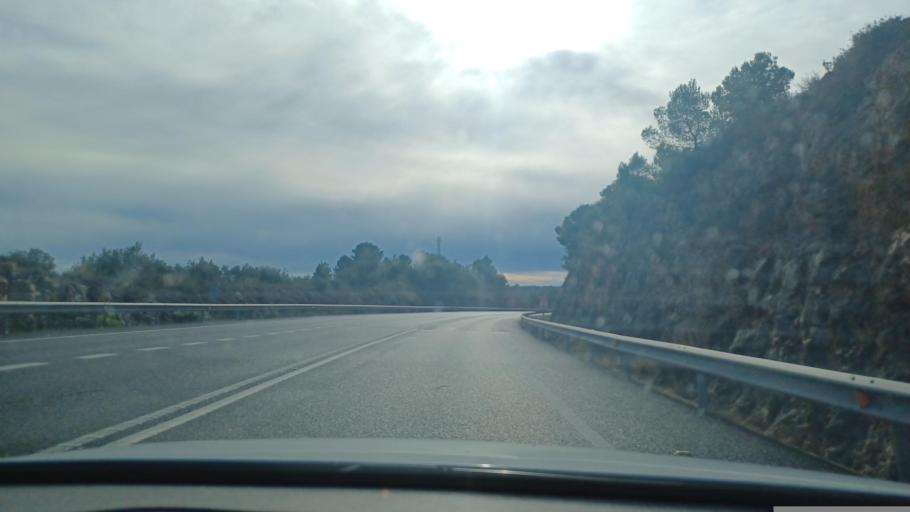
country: ES
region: Catalonia
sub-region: Provincia de Tarragona
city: El Perello
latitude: 40.8485
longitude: 0.7123
